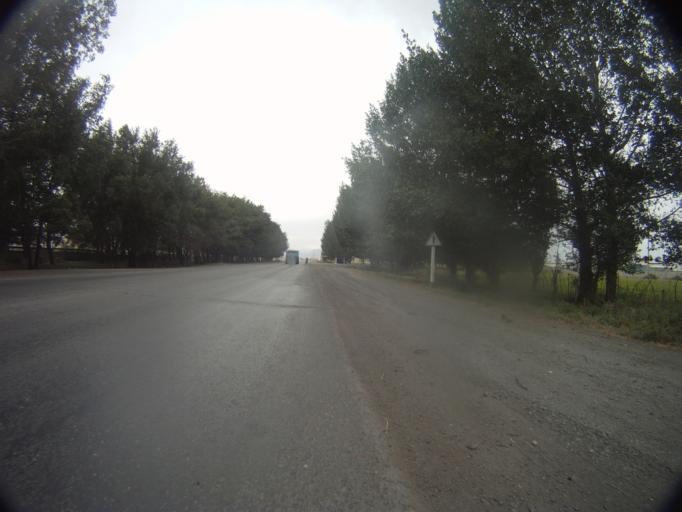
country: KG
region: Ysyk-Koel
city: Balykchy
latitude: 42.4372
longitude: 76.1421
